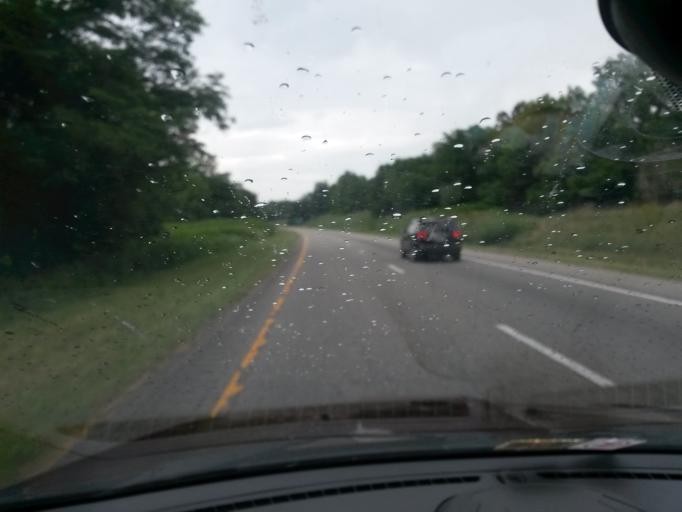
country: US
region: Virginia
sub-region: Rockbridge County
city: East Lexington
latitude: 37.8443
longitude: -79.4552
